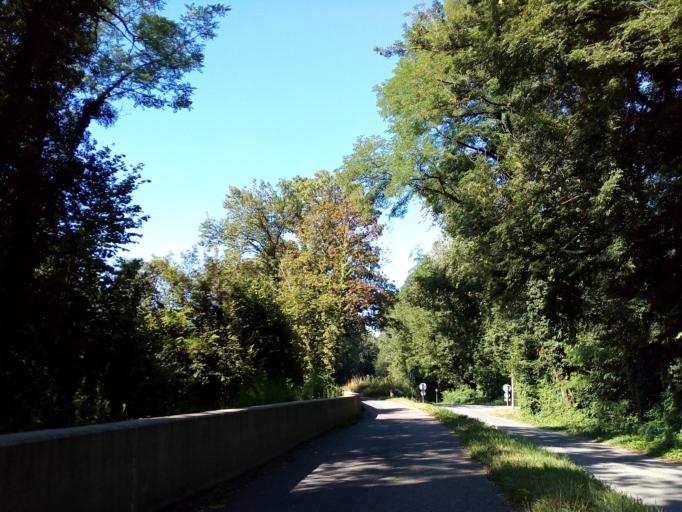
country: FR
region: Rhone-Alpes
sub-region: Departement de l'Isere
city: Le Versoud
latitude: 45.2214
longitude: 5.8422
